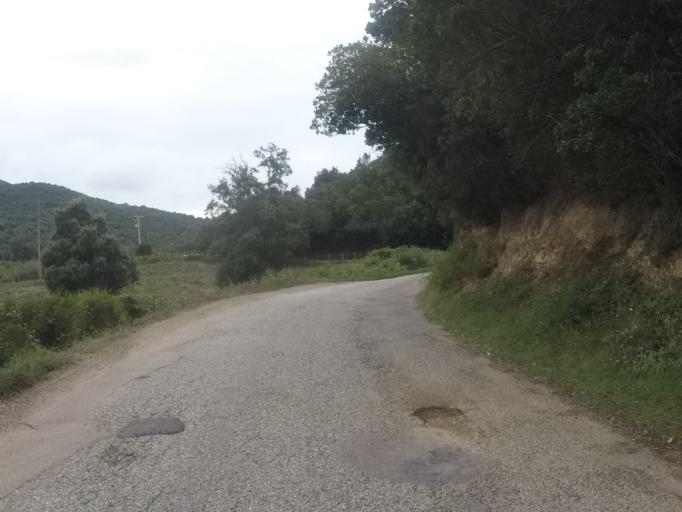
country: FR
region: Corsica
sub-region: Departement de la Corse-du-Sud
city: Pietrosella
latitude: 41.8131
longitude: 8.8505
